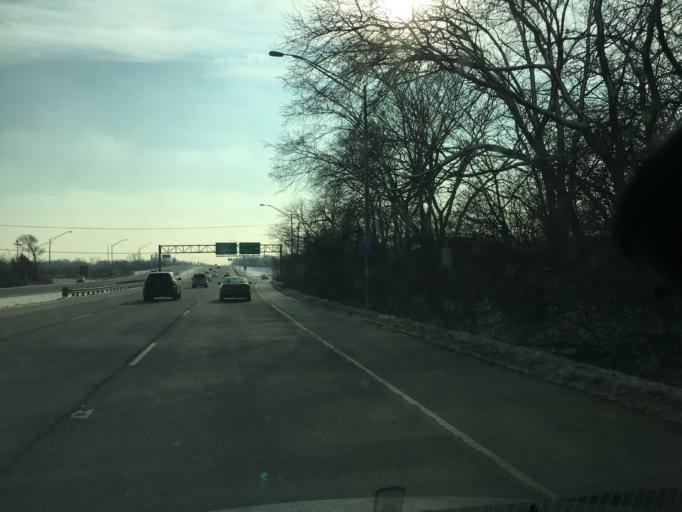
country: US
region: Illinois
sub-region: DuPage County
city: Willowbrook
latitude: 41.7462
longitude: -87.9448
